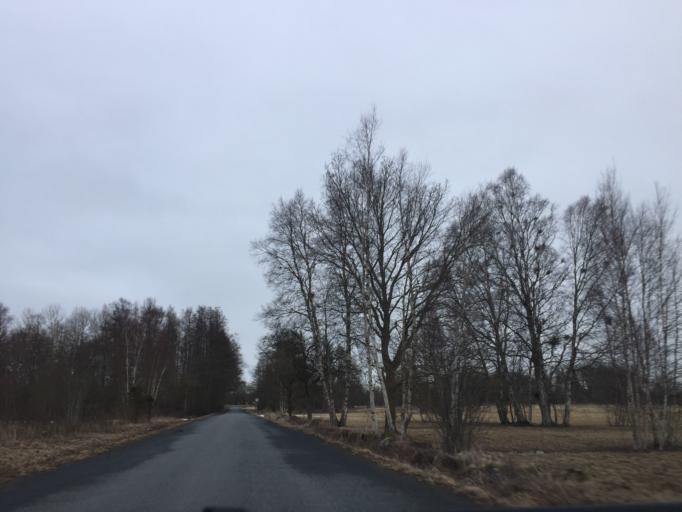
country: EE
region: Laeaene
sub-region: Haapsalu linn
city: Haapsalu
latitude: 58.7865
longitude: 23.4780
